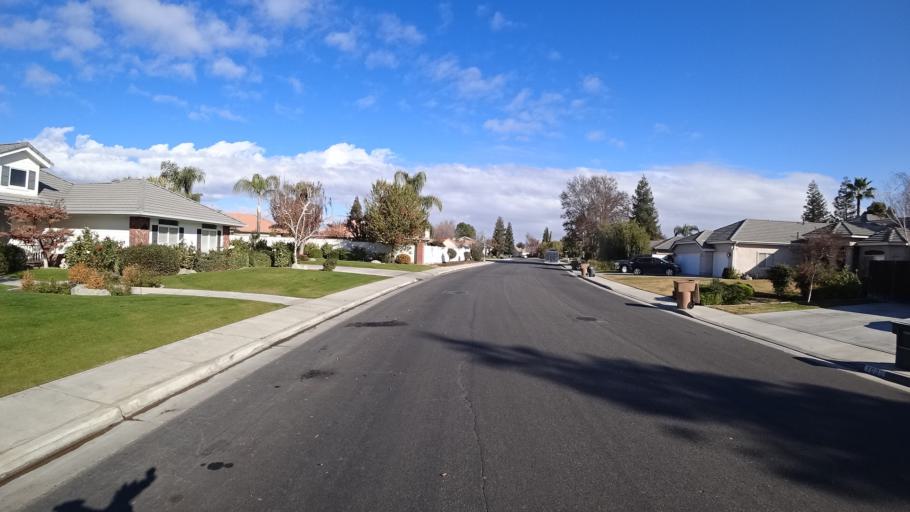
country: US
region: California
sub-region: Kern County
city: Greenacres
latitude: 35.3461
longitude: -119.1166
